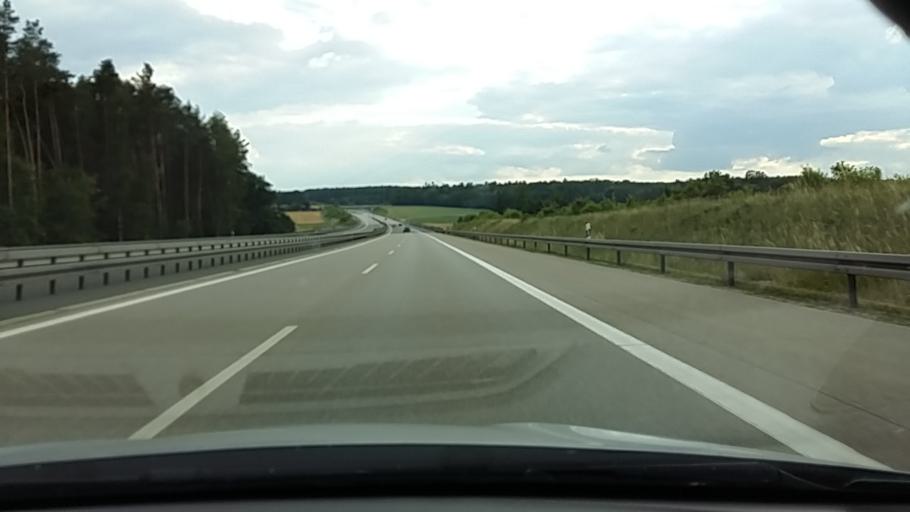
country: DE
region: Bavaria
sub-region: Upper Palatinate
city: Freudenberg
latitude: 49.4280
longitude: 12.0095
